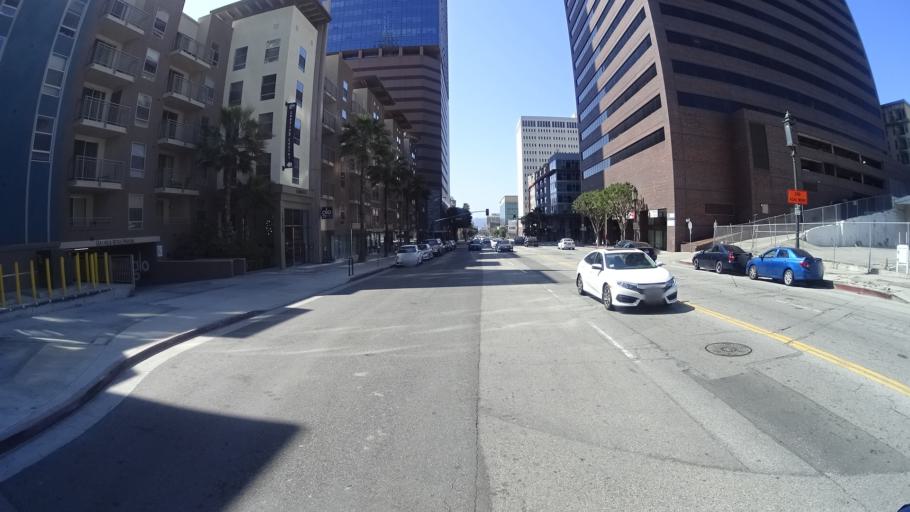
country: US
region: California
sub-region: Los Angeles County
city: Los Angeles
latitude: 34.0519
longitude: -118.2626
